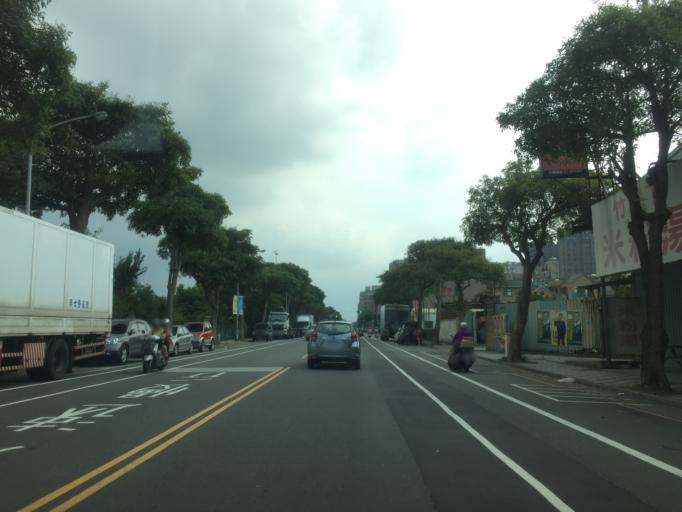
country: TW
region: Taiwan
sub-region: Taoyuan
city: Taoyuan
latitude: 24.9691
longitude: 121.3068
